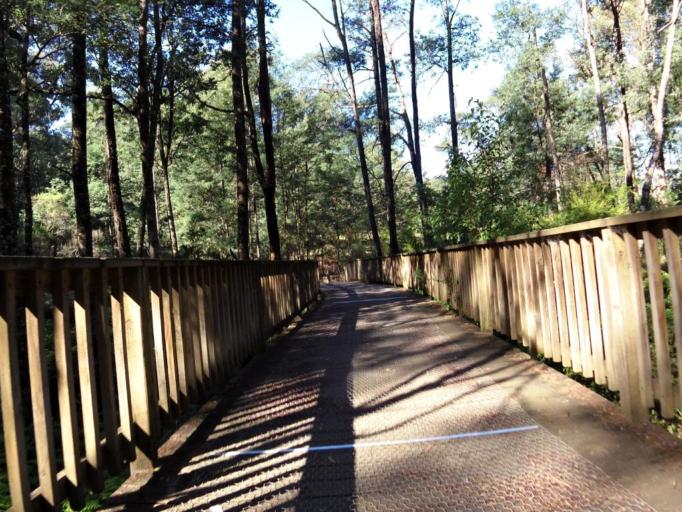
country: AU
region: Victoria
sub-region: Cardinia
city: Cockatoo
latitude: -37.9306
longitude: 145.4900
